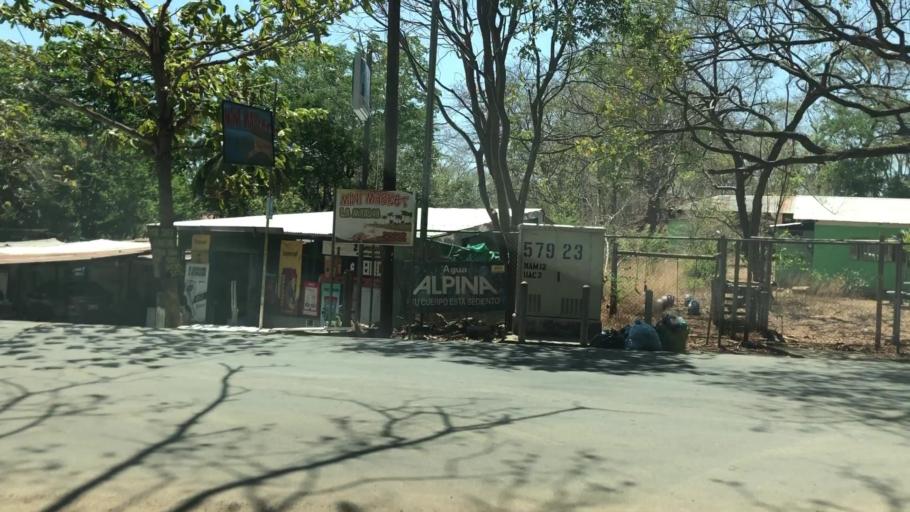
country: CR
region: Guanacaste
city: Sardinal
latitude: 10.3400
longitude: -85.8455
